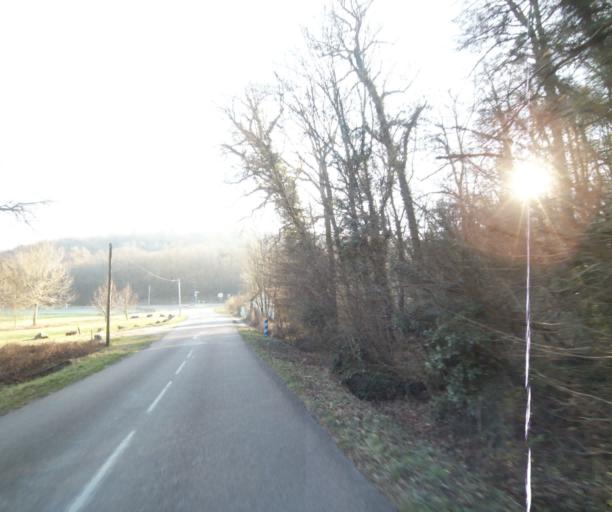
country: FR
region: Champagne-Ardenne
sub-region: Departement de la Haute-Marne
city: Bienville
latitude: 48.5560
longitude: 5.0869
